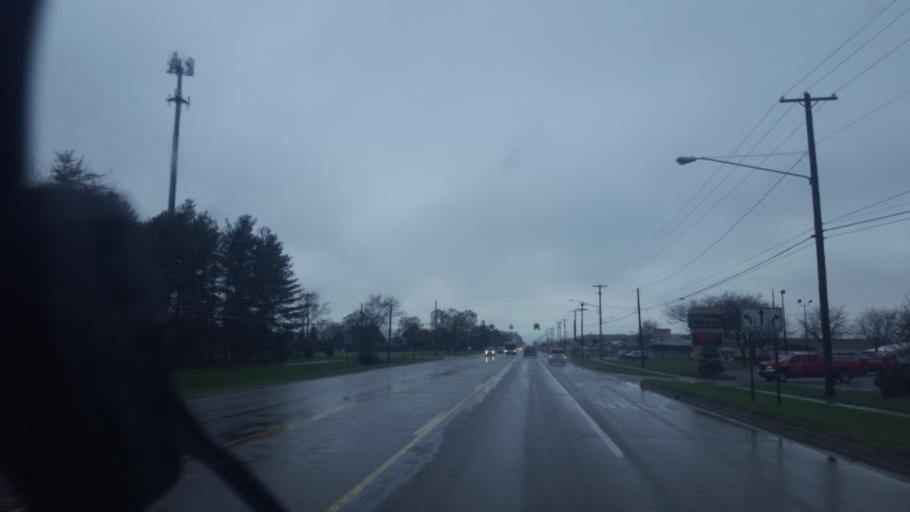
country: US
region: Michigan
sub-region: Isabella County
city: Mount Pleasant
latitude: 43.5971
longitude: -84.7960
